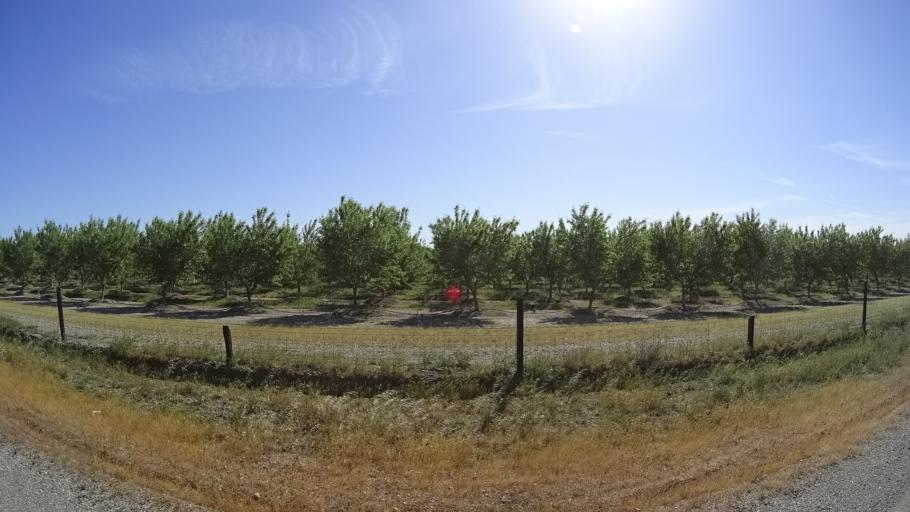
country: US
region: California
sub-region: Glenn County
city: Willows
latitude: 39.6264
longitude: -122.1601
